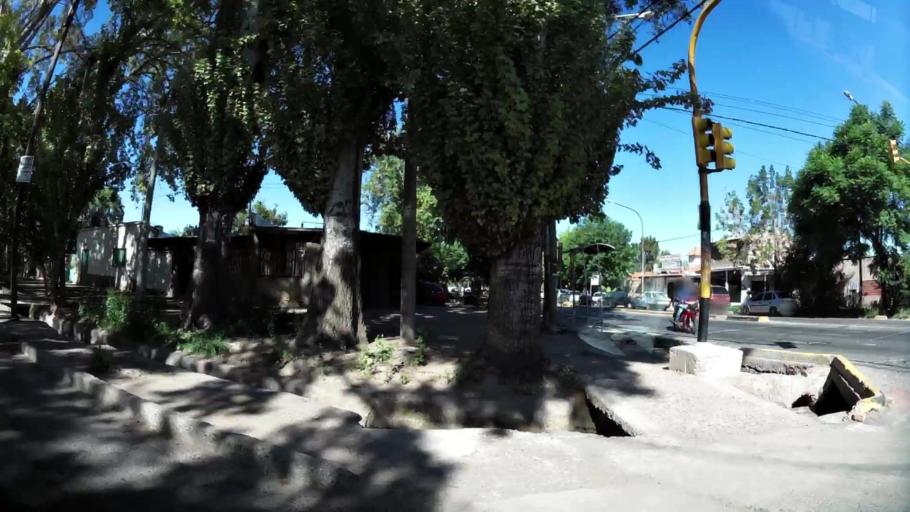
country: AR
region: Mendoza
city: Las Heras
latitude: -32.8418
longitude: -68.8266
